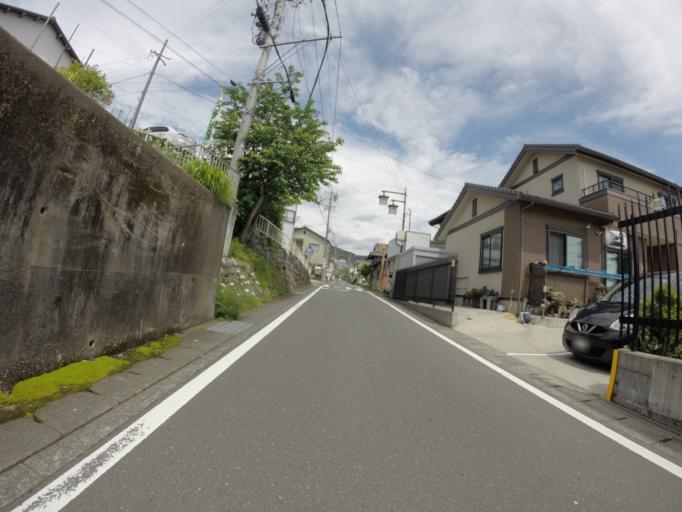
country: JP
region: Shizuoka
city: Fujinomiya
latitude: 35.1095
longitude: 138.5604
